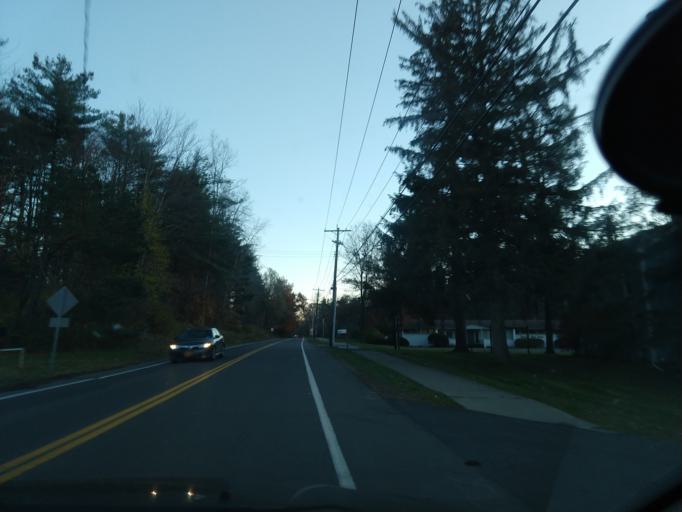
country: US
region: New York
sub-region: Tompkins County
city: Cayuga Heights
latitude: 42.4672
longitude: -76.4778
